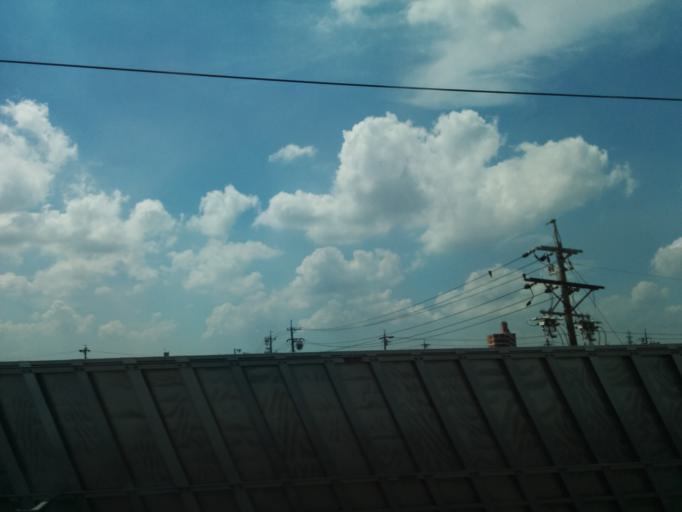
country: JP
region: Aichi
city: Inazawa
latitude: 35.2270
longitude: 136.8087
